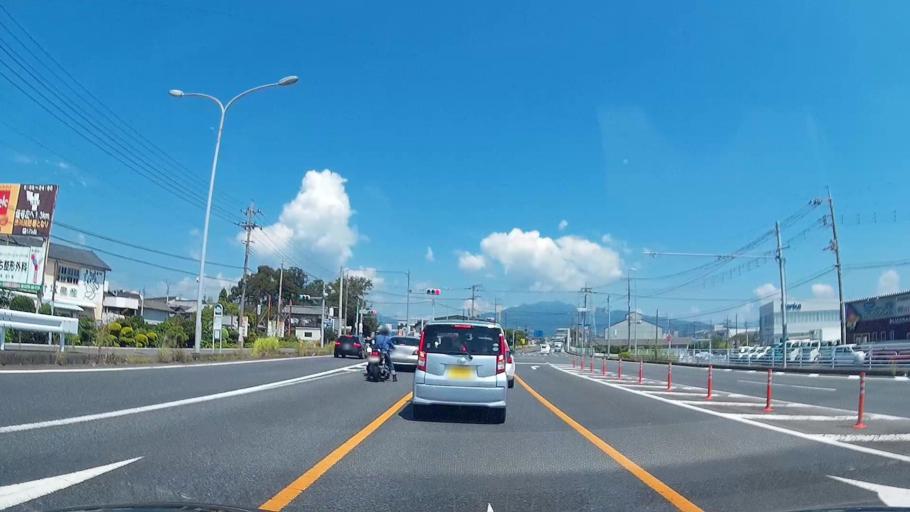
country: JP
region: Gunma
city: Shibukawa
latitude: 36.4847
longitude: 139.0125
